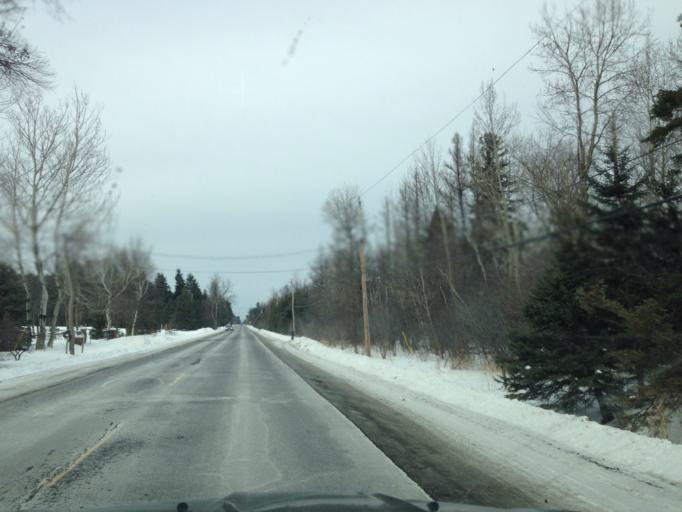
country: CA
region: Ontario
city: Ottawa
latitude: 45.3275
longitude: -75.5432
